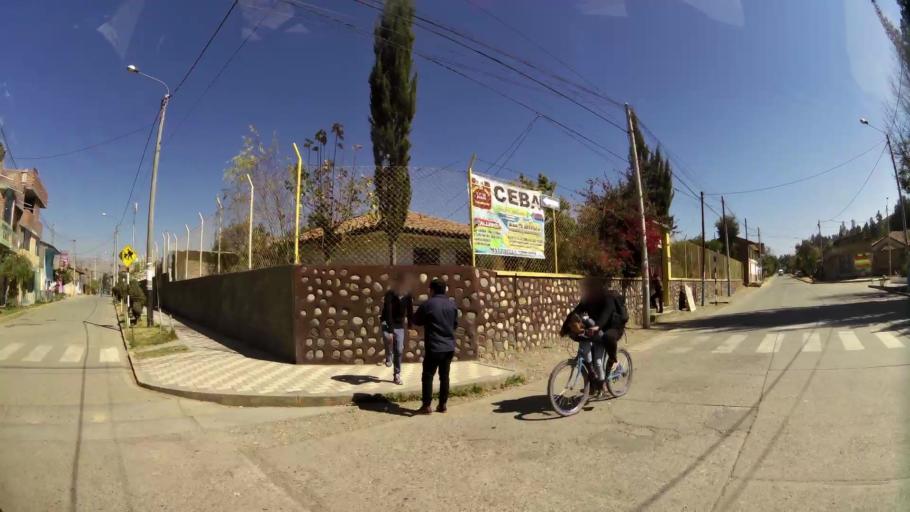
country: PE
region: Junin
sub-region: Provincia de Concepcion
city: Concepcion
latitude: -11.9141
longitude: -75.3165
